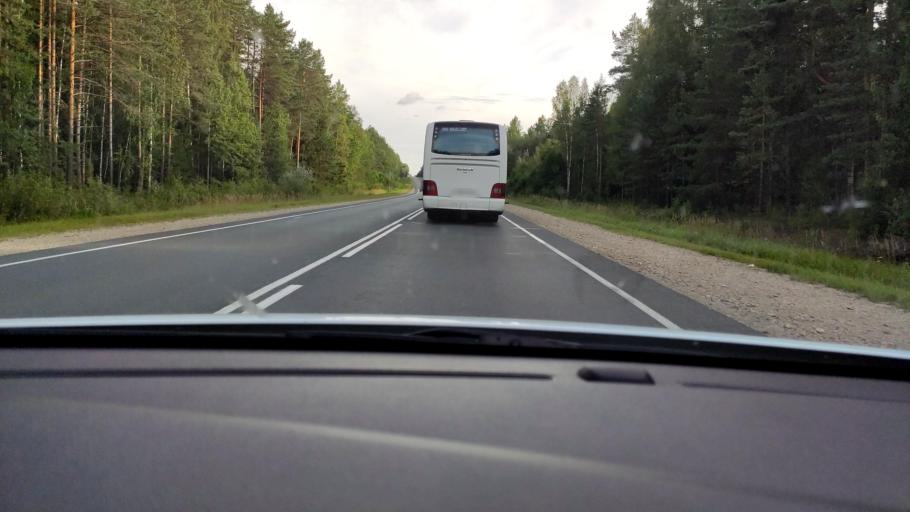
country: RU
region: Mariy-El
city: Suslonger
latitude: 56.2954
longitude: 48.2336
